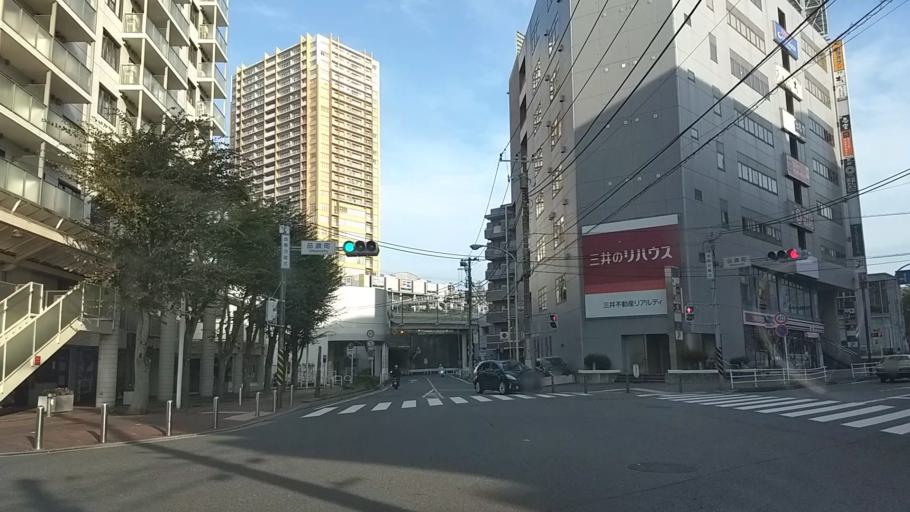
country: JP
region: Kanagawa
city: Yokohama
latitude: 35.4286
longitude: 139.5579
